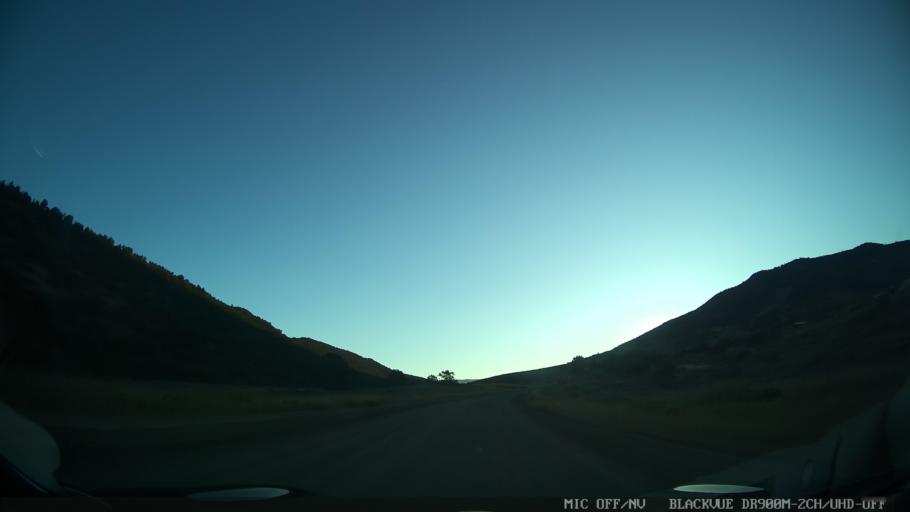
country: US
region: Colorado
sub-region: Grand County
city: Kremmling
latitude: 39.9093
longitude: -106.5781
